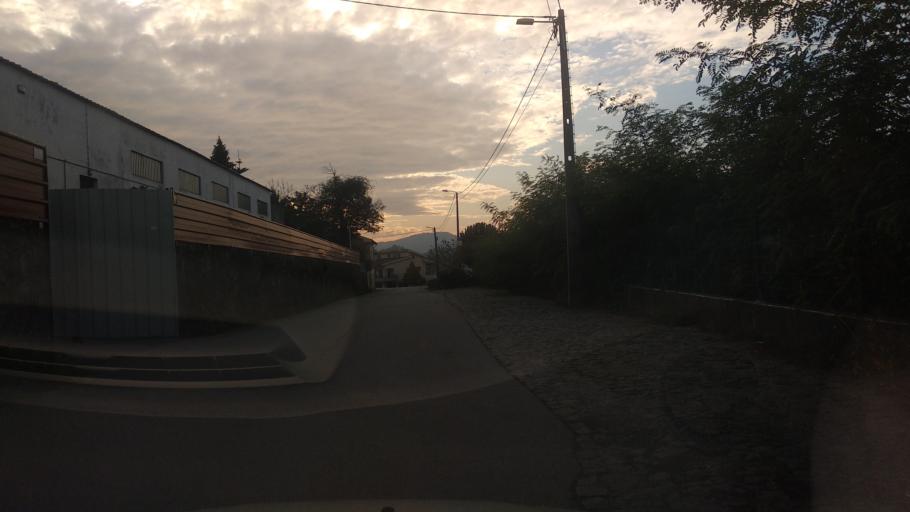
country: PT
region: Braga
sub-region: Braga
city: Braga
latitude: 41.5268
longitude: -8.4526
